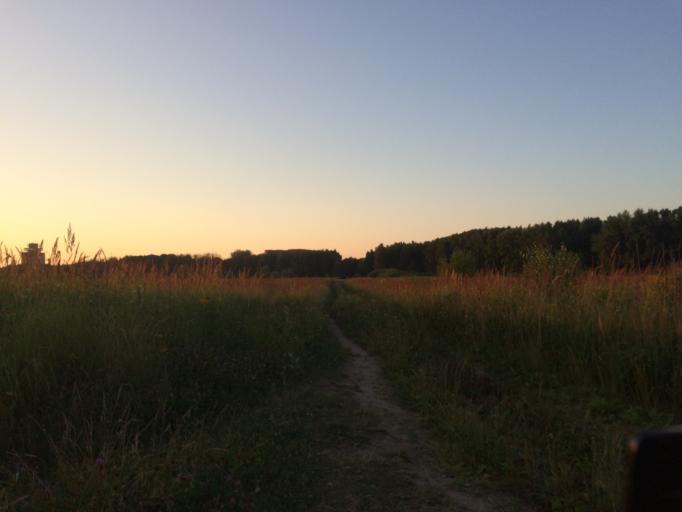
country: RU
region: Mariy-El
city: Yoshkar-Ola
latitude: 56.6189
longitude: 47.9172
